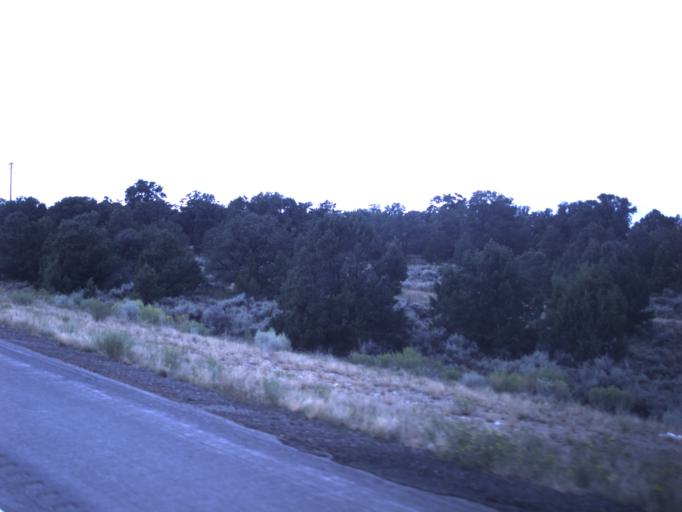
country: US
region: Utah
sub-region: Duchesne County
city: Duchesne
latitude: 40.1814
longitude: -110.6427
